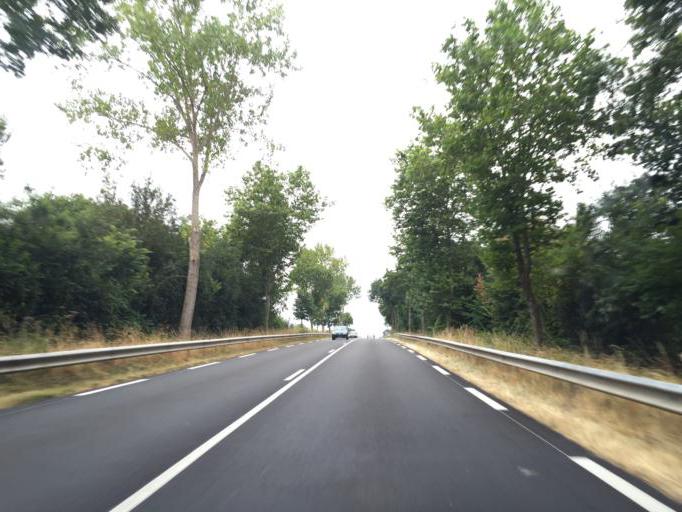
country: FR
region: Auvergne
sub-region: Departement de l'Allier
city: Brout-Vernet
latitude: 46.1998
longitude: 3.2726
